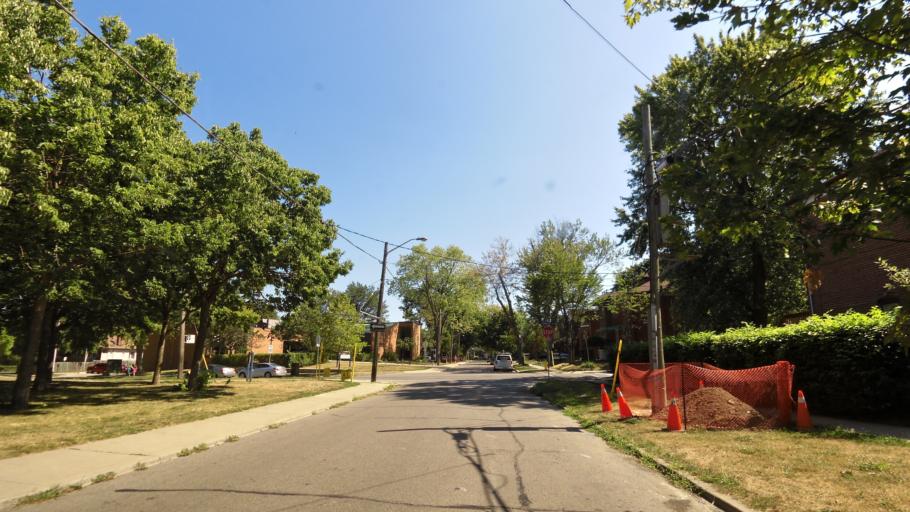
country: CA
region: Ontario
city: Etobicoke
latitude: 43.6153
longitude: -79.4944
